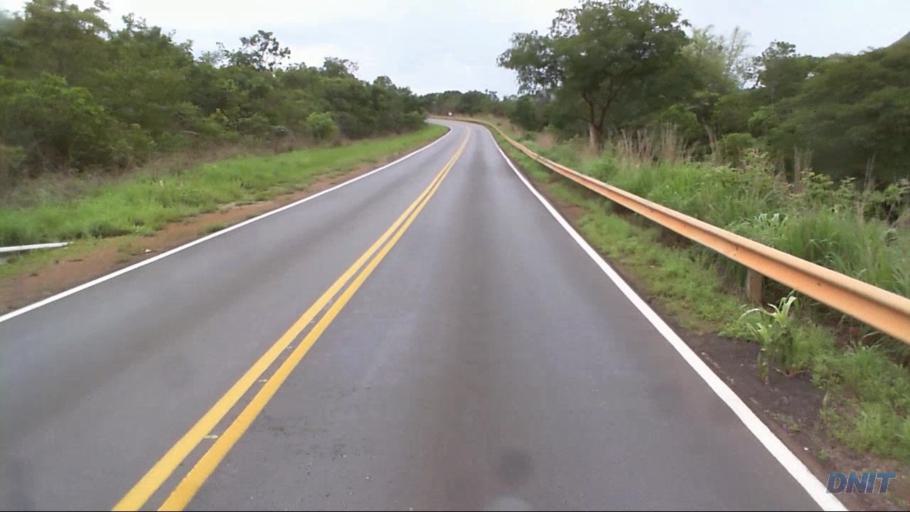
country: BR
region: Goias
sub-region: Padre Bernardo
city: Padre Bernardo
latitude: -15.4126
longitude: -48.2006
